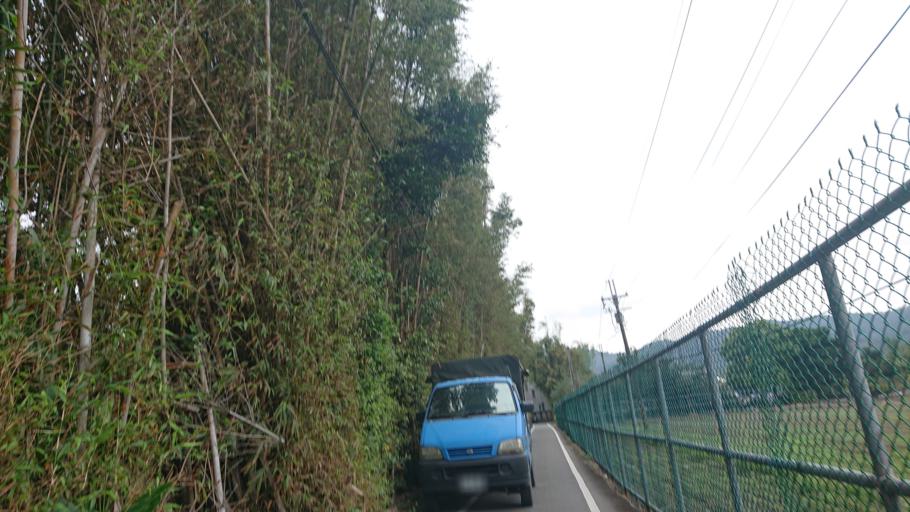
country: TW
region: Taiwan
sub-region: Taoyuan
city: Taoyuan
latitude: 24.9480
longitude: 121.3653
